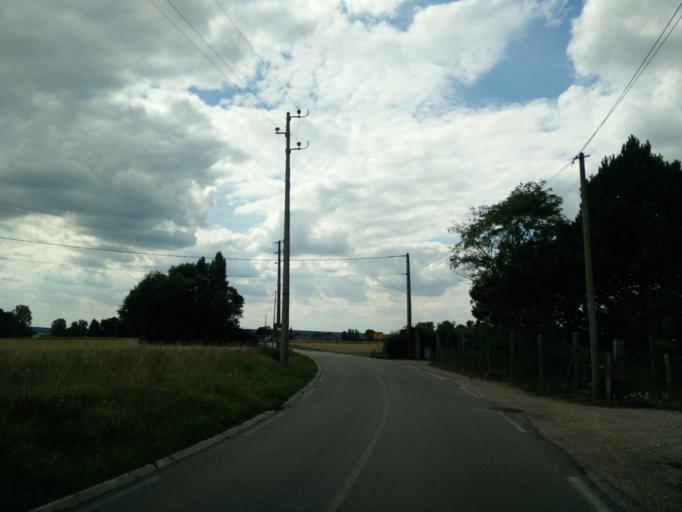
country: FR
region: Ile-de-France
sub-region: Departement des Yvelines
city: Thoiry
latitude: 48.8543
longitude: 1.7716
